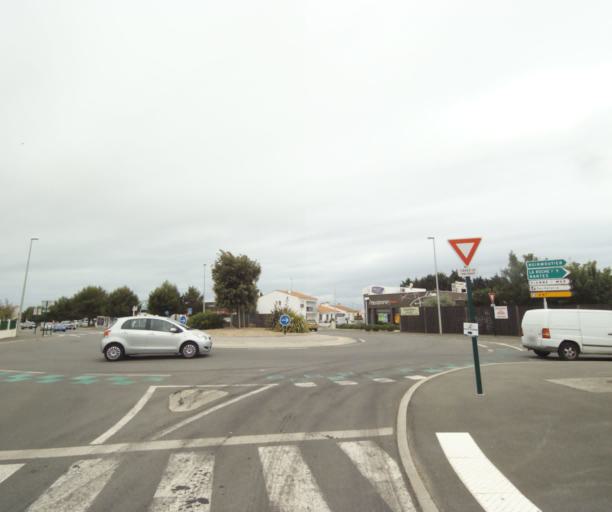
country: FR
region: Pays de la Loire
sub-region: Departement de la Vendee
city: Chateau-d'Olonne
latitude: 46.4956
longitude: -1.7522
